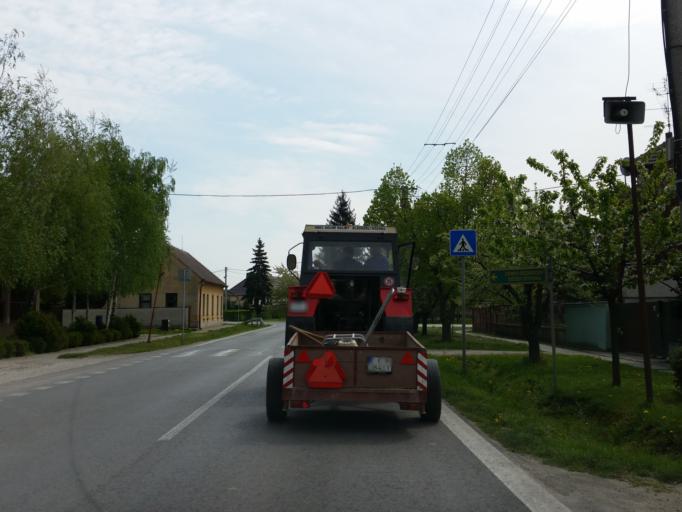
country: SK
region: Trnavsky
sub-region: Okres Galanta
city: Galanta
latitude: 48.1072
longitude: 17.7843
